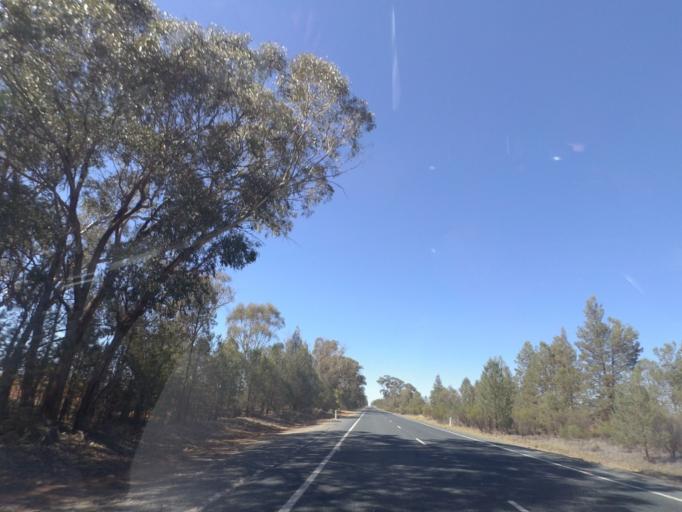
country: AU
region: New South Wales
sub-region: Bland
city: West Wyalong
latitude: -34.1520
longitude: 147.1183
